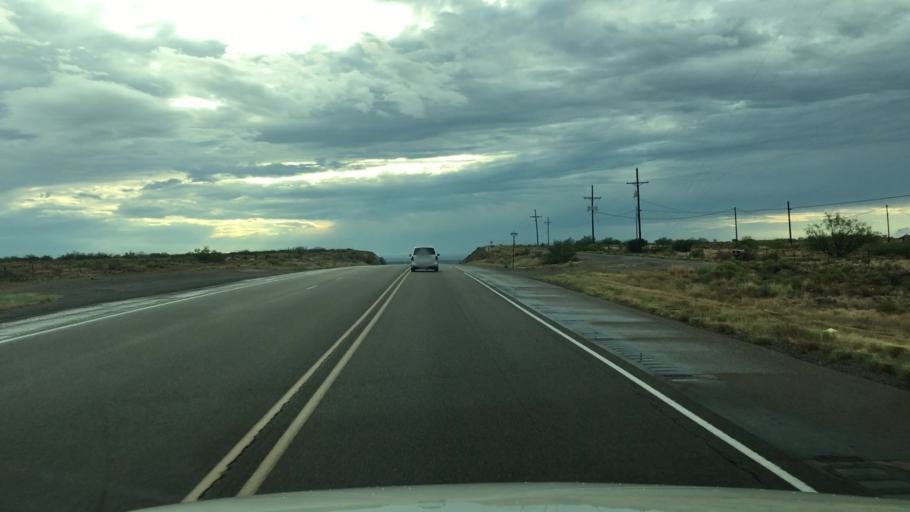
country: US
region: New Mexico
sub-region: Chaves County
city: Roswell
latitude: 33.3963
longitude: -104.3746
